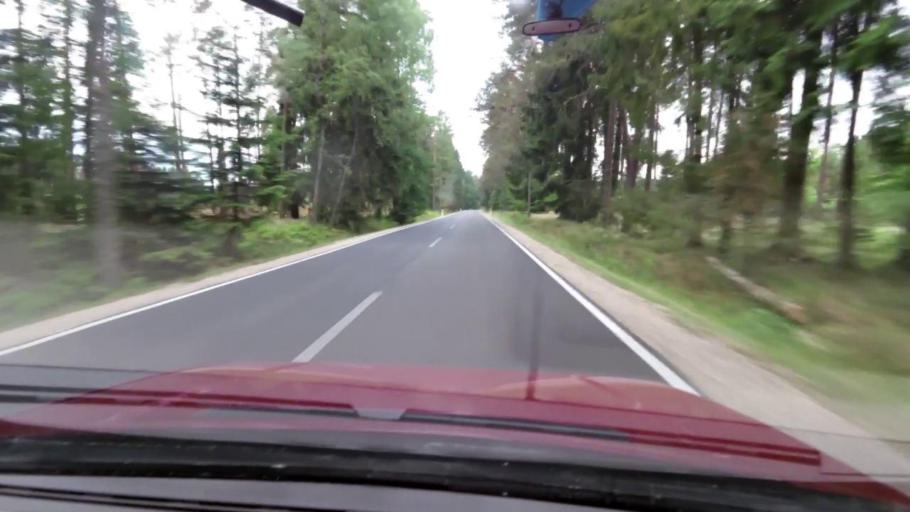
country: PL
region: West Pomeranian Voivodeship
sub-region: Powiat koszalinski
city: Polanow
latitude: 54.1449
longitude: 16.4807
